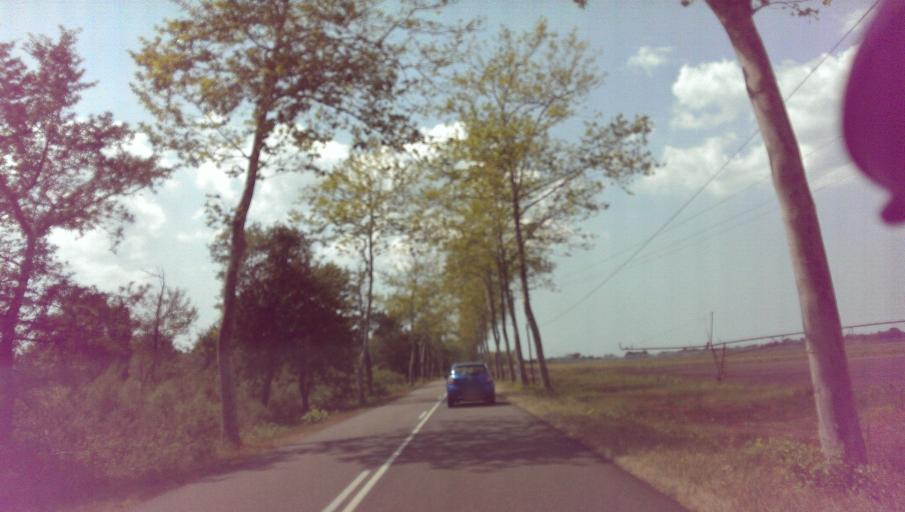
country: FR
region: Aquitaine
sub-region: Departement des Landes
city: Sabres
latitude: 44.1190
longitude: -0.6451
